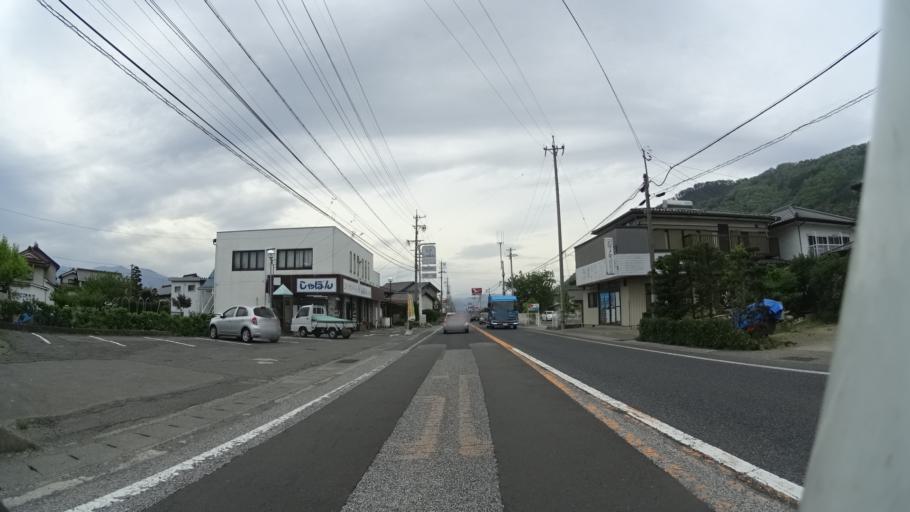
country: JP
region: Nagano
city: Nagano-shi
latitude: 36.5078
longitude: 138.1397
